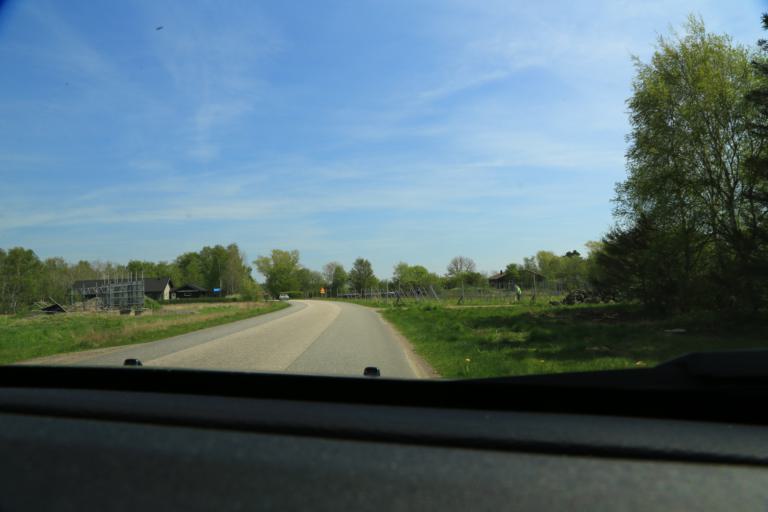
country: SE
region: Halland
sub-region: Varbergs Kommun
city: Varberg
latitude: 57.1459
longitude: 12.2420
